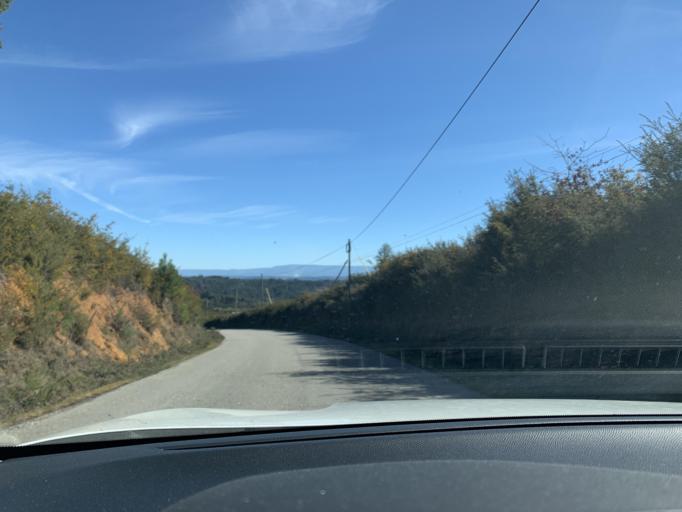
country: PT
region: Viseu
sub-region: Concelho de Tondela
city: Tondela
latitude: 40.6050
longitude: -8.0414
